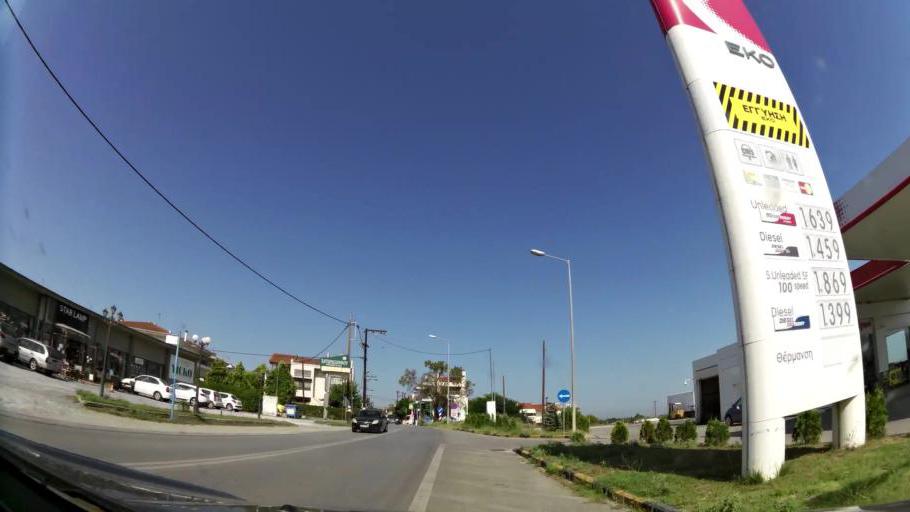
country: GR
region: Central Macedonia
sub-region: Nomos Thessalonikis
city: Neo Rysi
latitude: 40.4970
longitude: 22.9921
